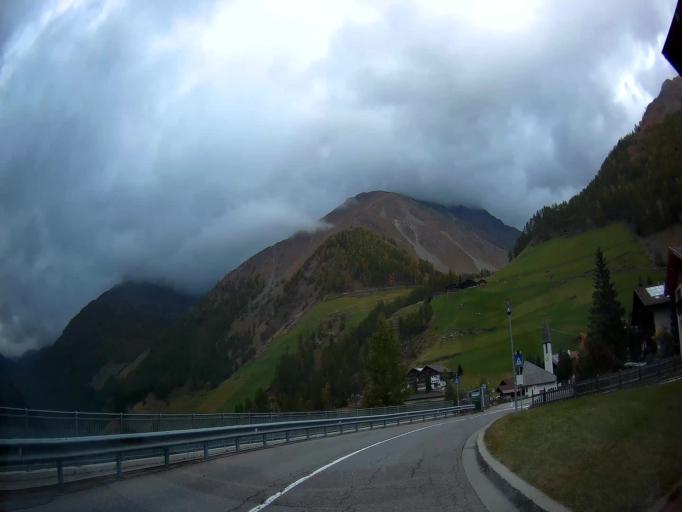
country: IT
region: Trentino-Alto Adige
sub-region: Bolzano
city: Senales
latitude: 46.7354
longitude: 10.8497
